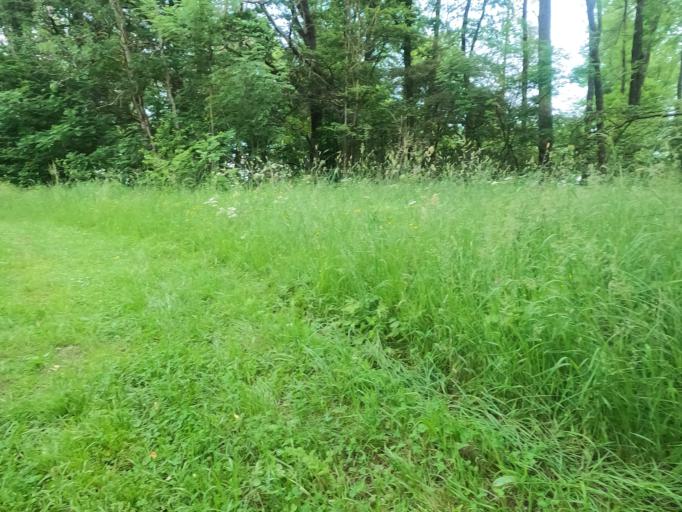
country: DE
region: Rheinland-Pfalz
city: Lochum
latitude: 50.6187
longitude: 7.8620
